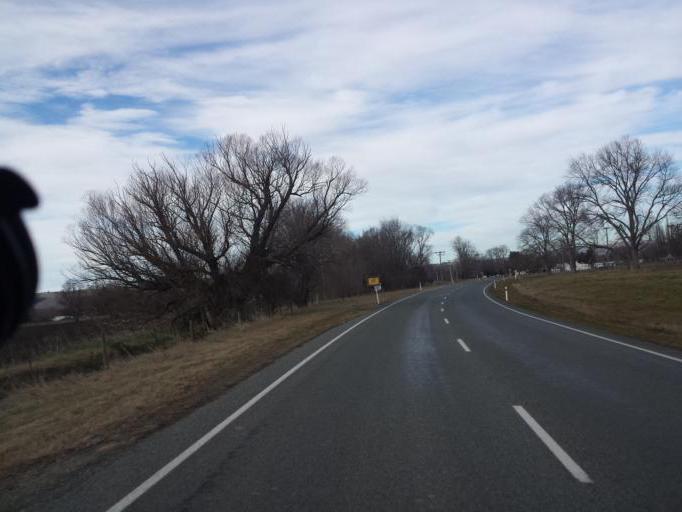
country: NZ
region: Canterbury
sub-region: Timaru District
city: Pleasant Point
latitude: -44.0848
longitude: 170.8127
